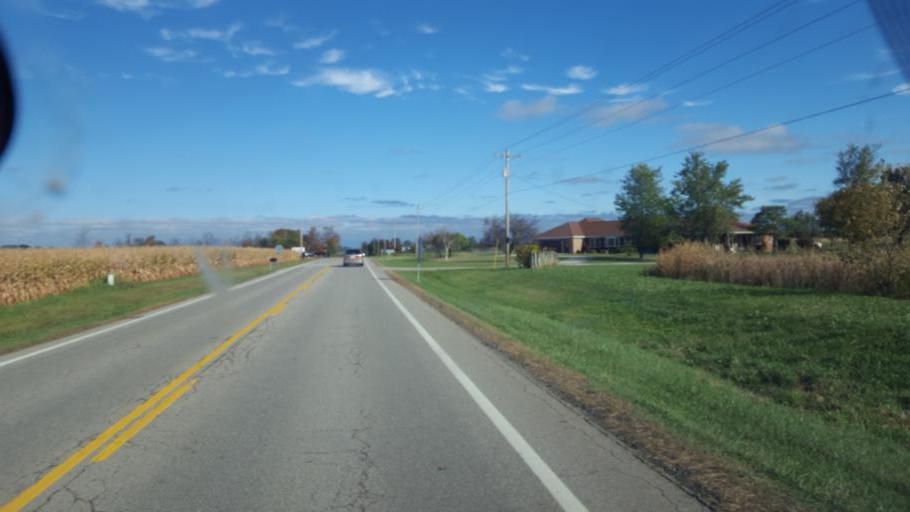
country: US
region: Ohio
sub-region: Huron County
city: Greenwich
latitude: 41.0396
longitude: -82.4858
